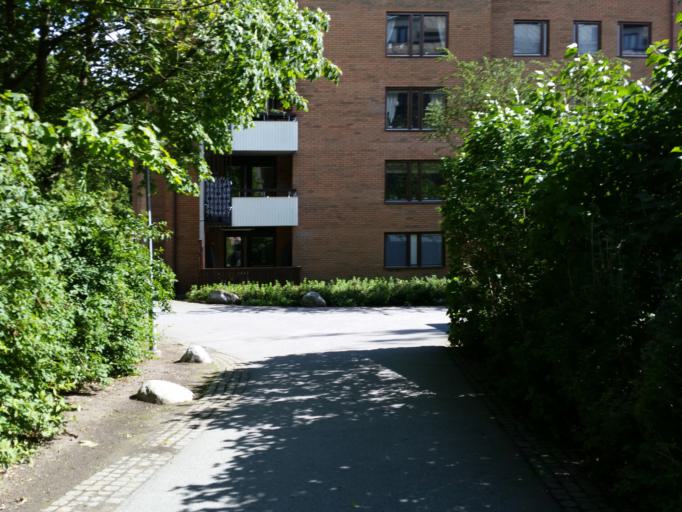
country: SE
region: Stockholm
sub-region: Solna Kommun
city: Solna
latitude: 59.3650
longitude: 18.0000
